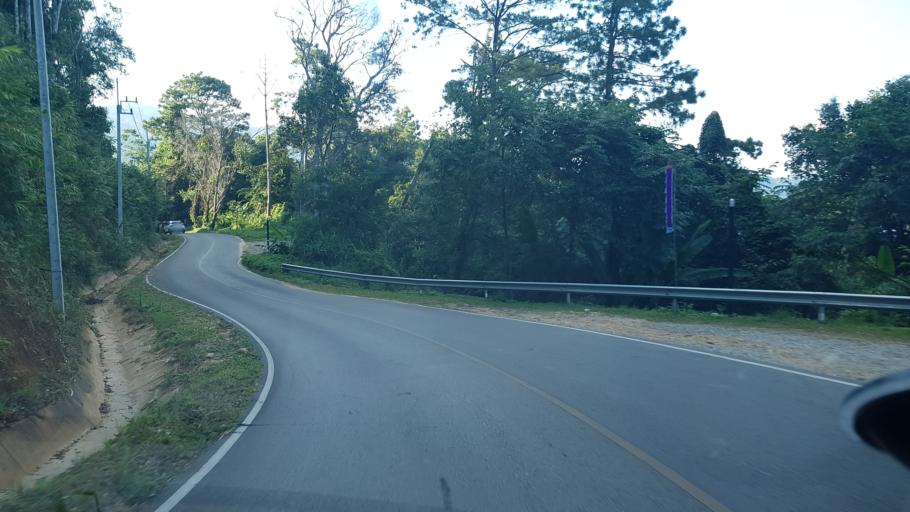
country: TH
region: Chiang Rai
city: Mae Fa Luang
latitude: 20.3280
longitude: 99.8286
